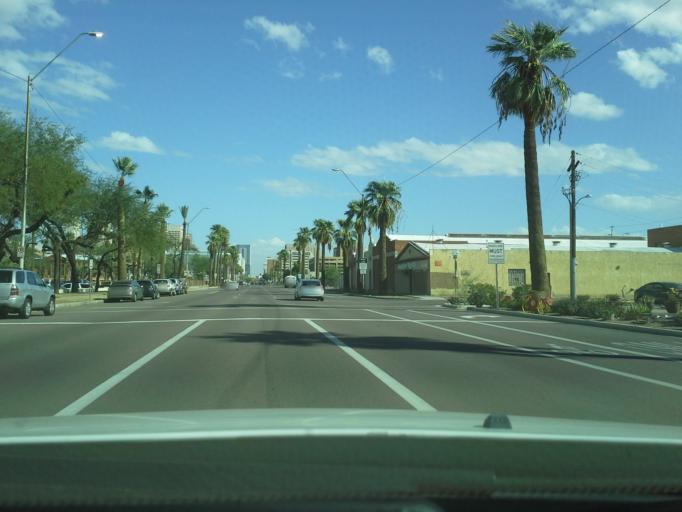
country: US
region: Arizona
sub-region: Maricopa County
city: Phoenix
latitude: 33.4471
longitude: -112.0898
